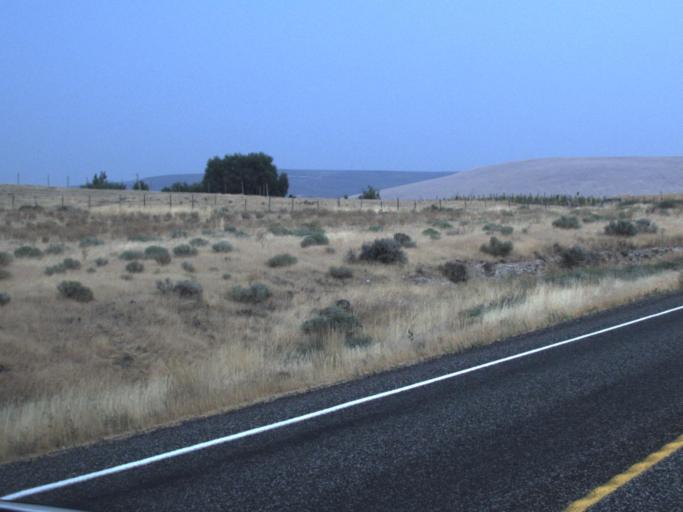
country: US
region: Washington
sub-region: Grant County
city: Desert Aire
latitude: 46.5077
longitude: -119.8798
